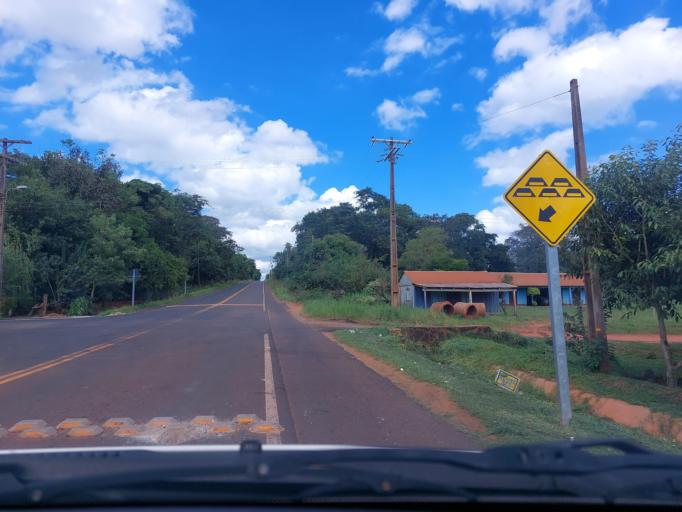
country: PY
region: San Pedro
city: Guayaybi
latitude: -24.5499
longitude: -56.5196
